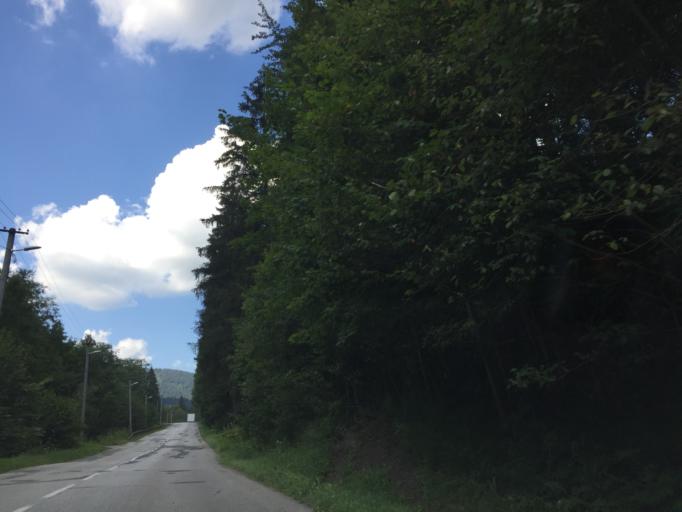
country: SK
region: Zilinsky
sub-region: Okres Dolny Kubin
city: Dolny Kubin
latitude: 49.2680
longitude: 19.3533
